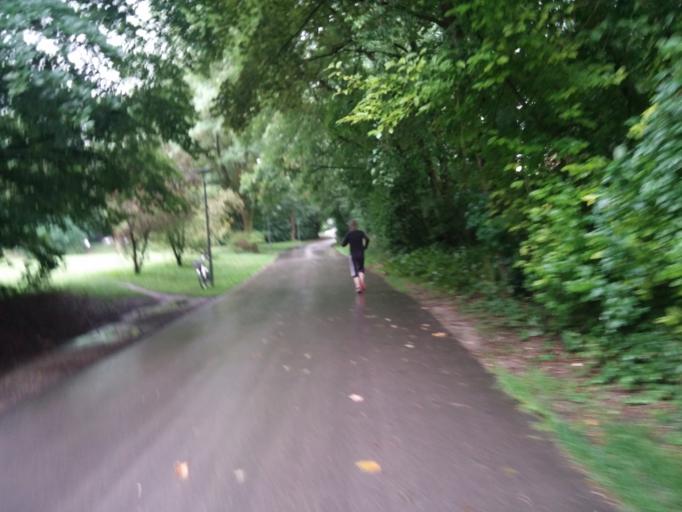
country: DE
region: Bavaria
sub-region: Upper Bavaria
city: Munich
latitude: 48.0968
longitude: 11.5593
